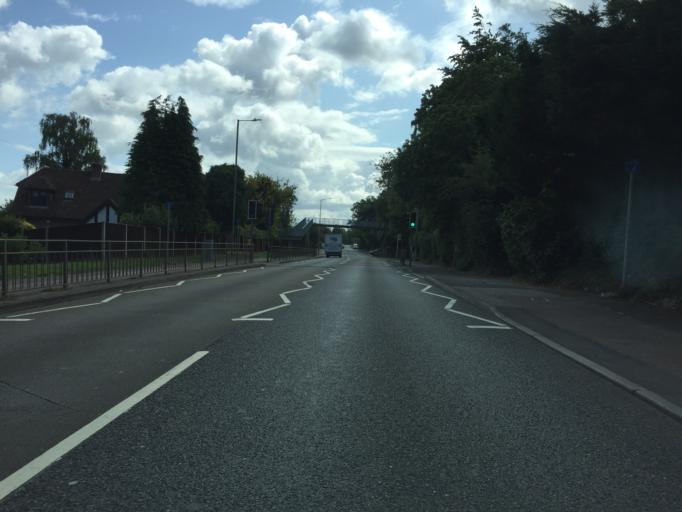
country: GB
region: England
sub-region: Kent
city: Aylesford
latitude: 51.2967
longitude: 0.4639
